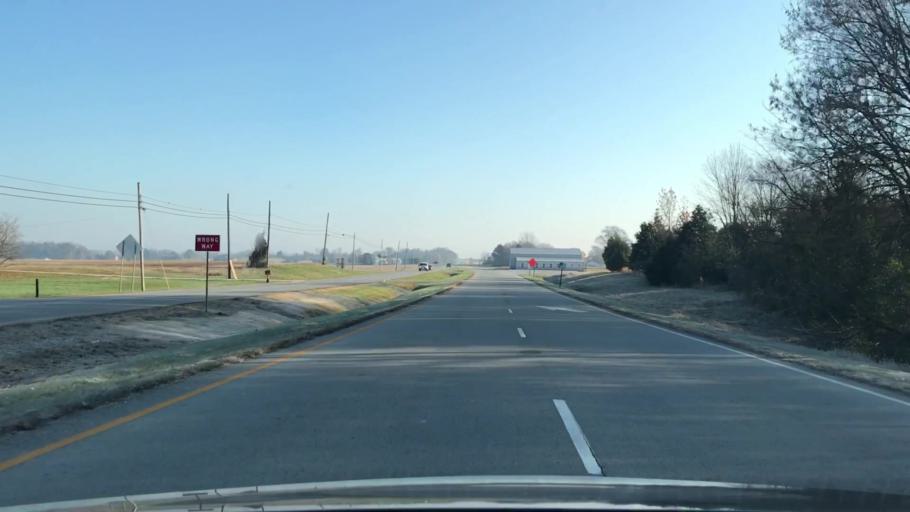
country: US
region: Kentucky
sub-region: Warren County
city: Bowling Green
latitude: 37.0394
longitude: -86.3322
